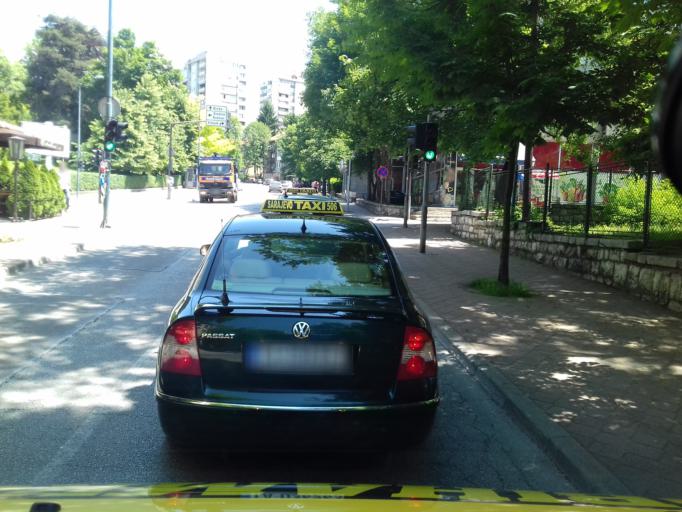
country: BA
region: Federation of Bosnia and Herzegovina
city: Kobilja Glava
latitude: 43.8669
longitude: 18.4155
